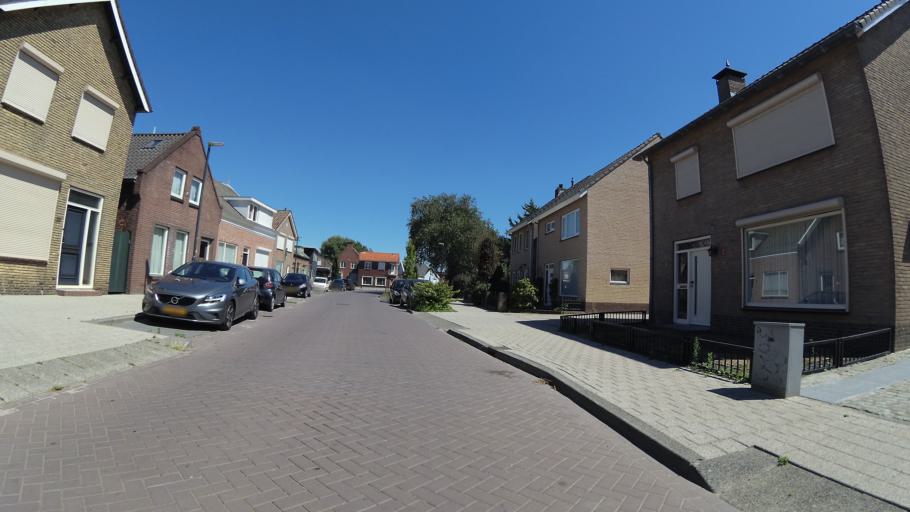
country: NL
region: North Brabant
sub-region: Gemeente Waalwijk
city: Waalwijk
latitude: 51.6838
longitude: 5.0667
